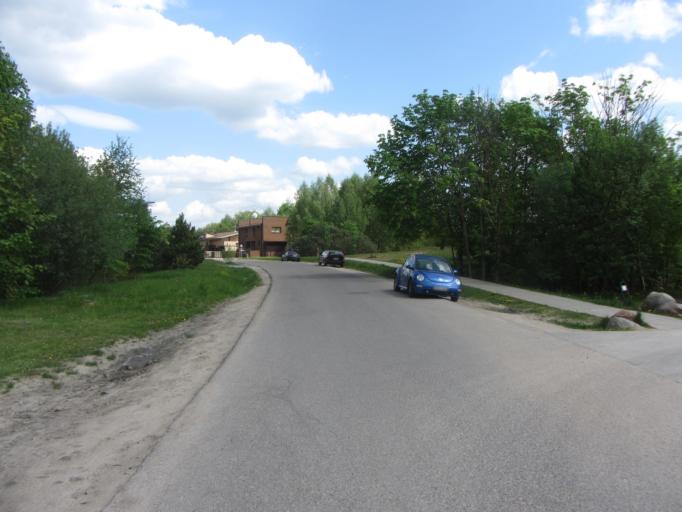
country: LT
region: Vilnius County
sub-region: Vilnius
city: Fabijoniskes
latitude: 54.7568
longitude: 25.2815
